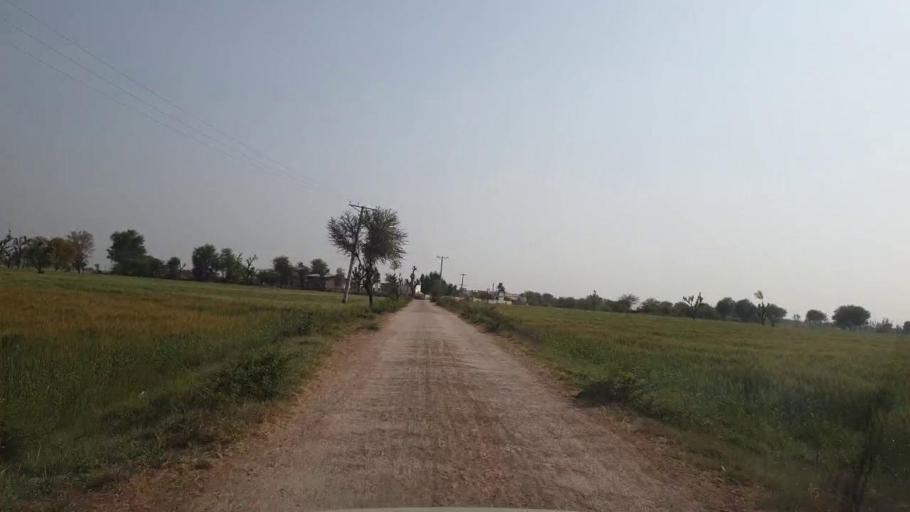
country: PK
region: Sindh
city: Dhoro Naro
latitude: 25.4741
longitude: 69.6465
